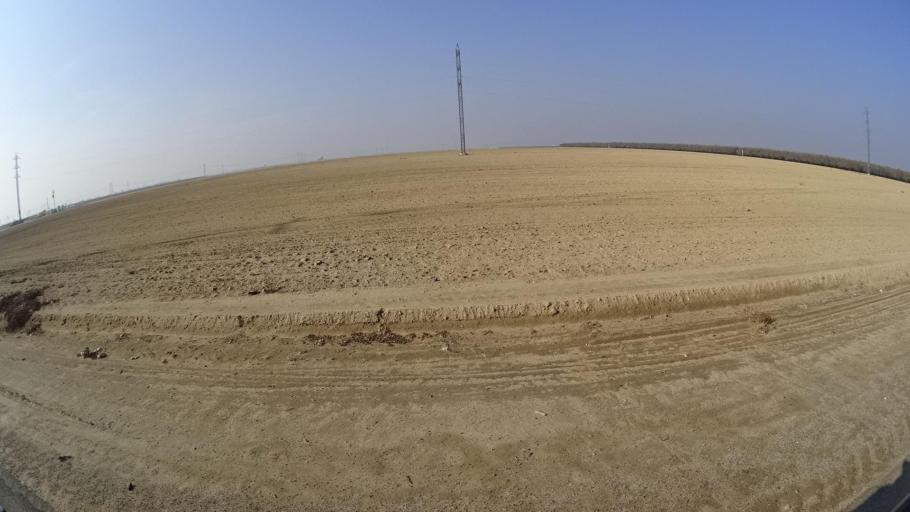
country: US
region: California
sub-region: Kern County
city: Buttonwillow
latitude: 35.4186
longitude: -119.4471
